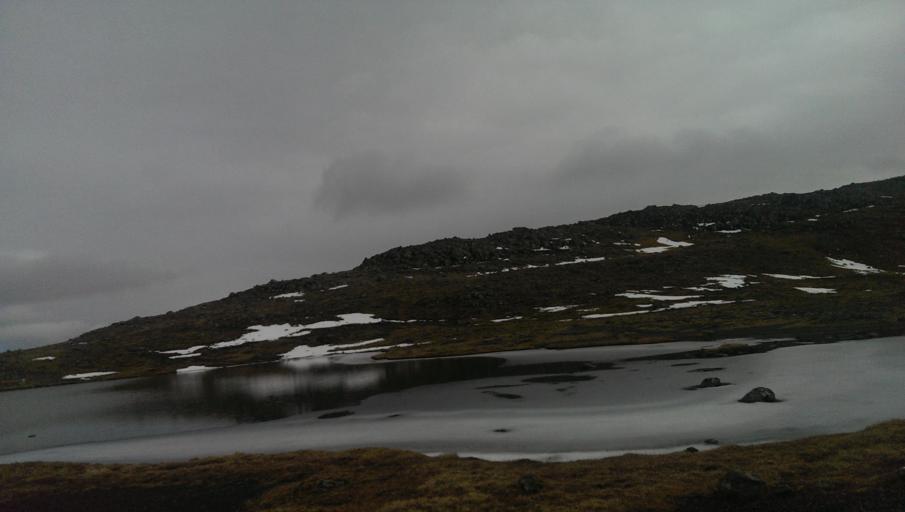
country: FO
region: Streymoy
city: Kollafjordhur
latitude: 62.0303
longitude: -6.8876
